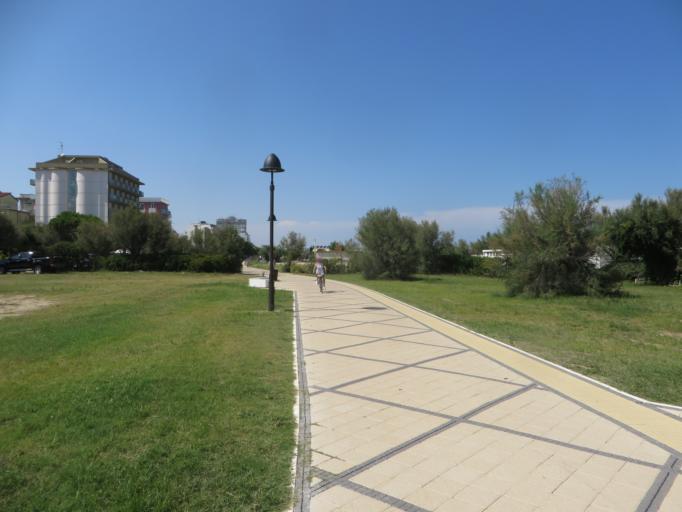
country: IT
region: Emilia-Romagna
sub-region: Provincia di Ravenna
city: Cervia
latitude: 44.2714
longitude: 12.3553
